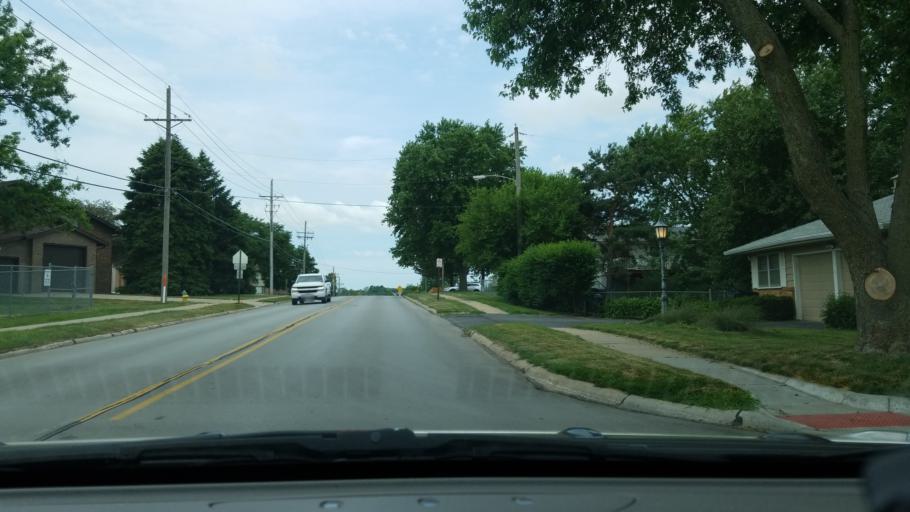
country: US
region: Nebraska
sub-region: Sarpy County
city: Papillion
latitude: 41.1436
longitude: -96.0388
